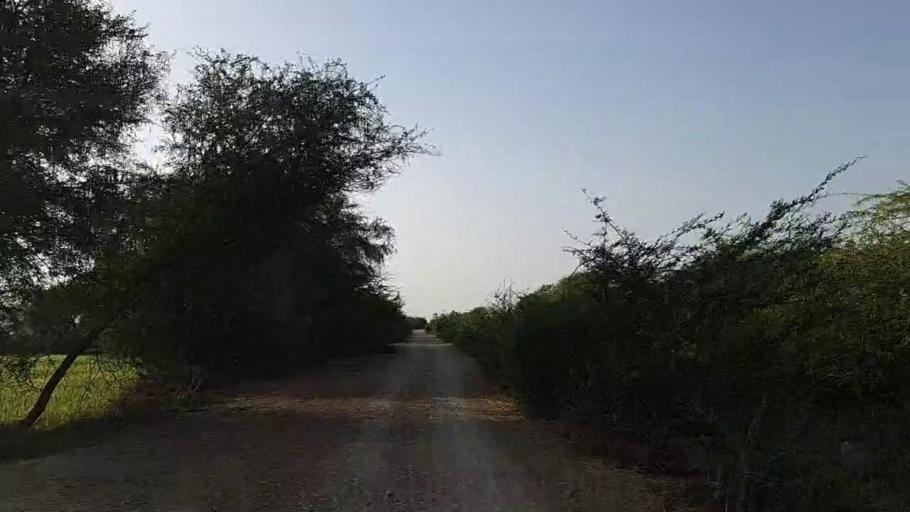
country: PK
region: Sindh
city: Jati
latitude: 24.3412
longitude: 68.1478
